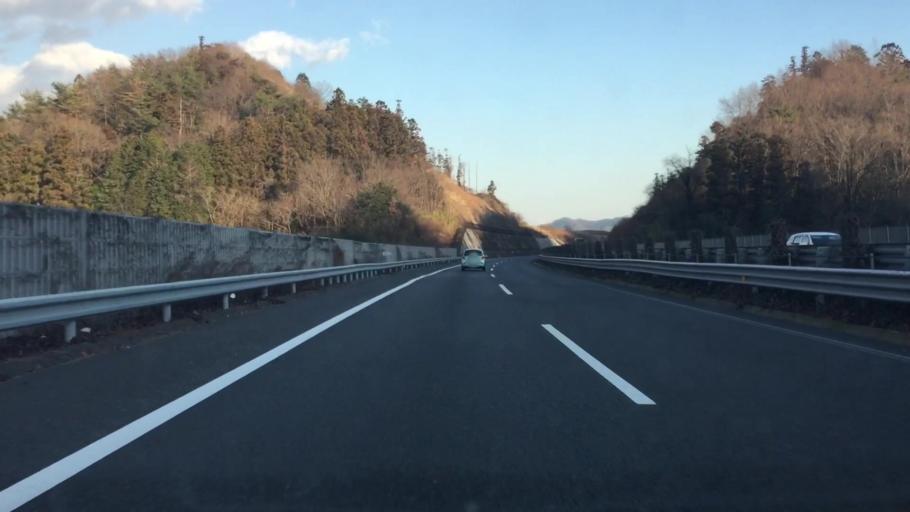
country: JP
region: Tochigi
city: Tanuma
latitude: 36.3741
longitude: 139.5310
